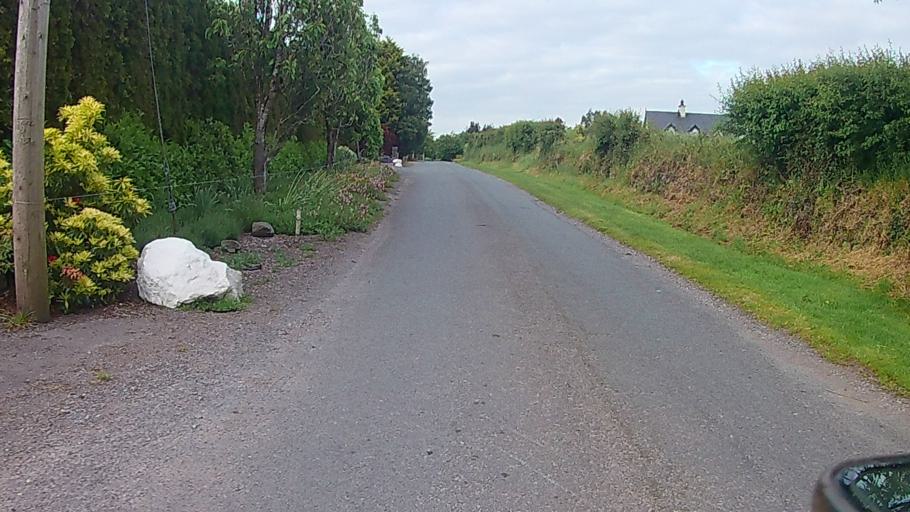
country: IE
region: Munster
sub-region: County Cork
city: Watergrasshill
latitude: 51.9771
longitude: -8.4105
